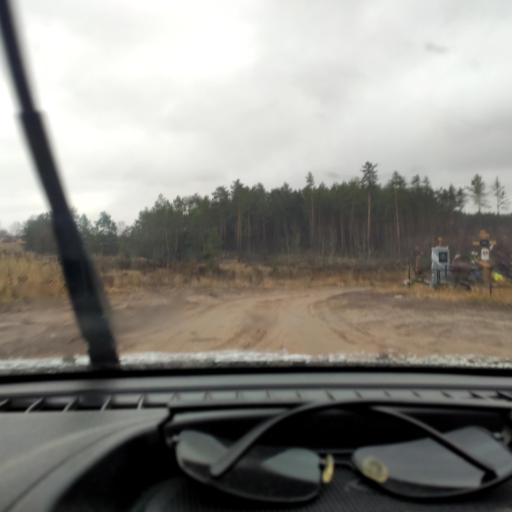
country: RU
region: Samara
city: Zhigulevsk
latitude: 53.5393
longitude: 49.5545
